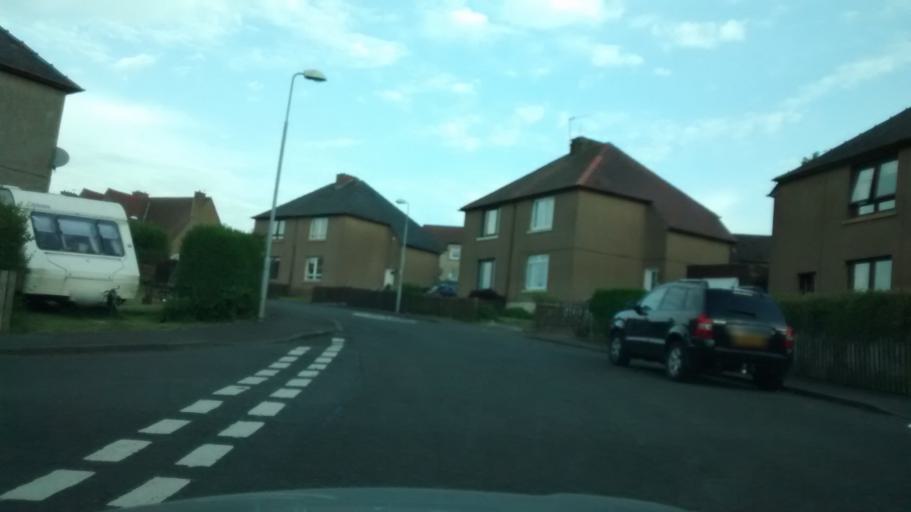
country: GB
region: Scotland
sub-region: West Lothian
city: Armadale
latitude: 55.8971
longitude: -3.7081
